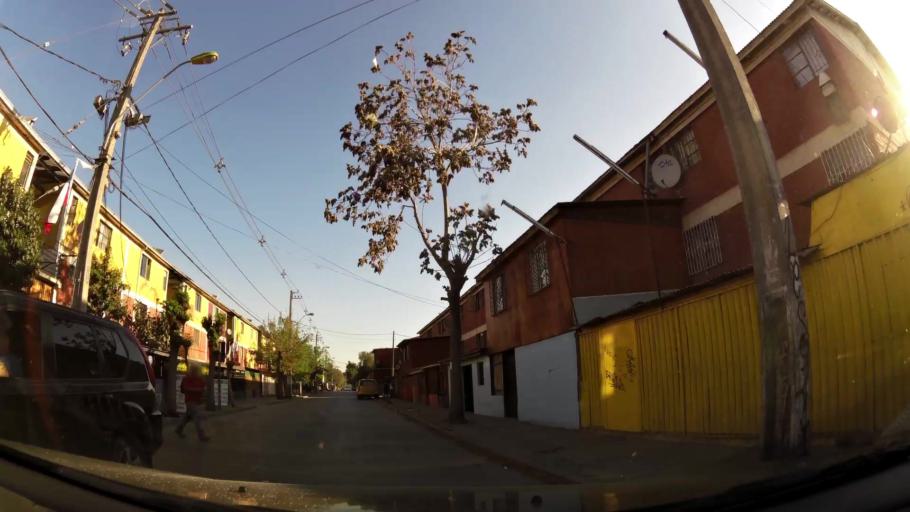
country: CL
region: Santiago Metropolitan
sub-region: Provincia de Santiago
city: La Pintana
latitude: -33.5774
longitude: -70.6635
